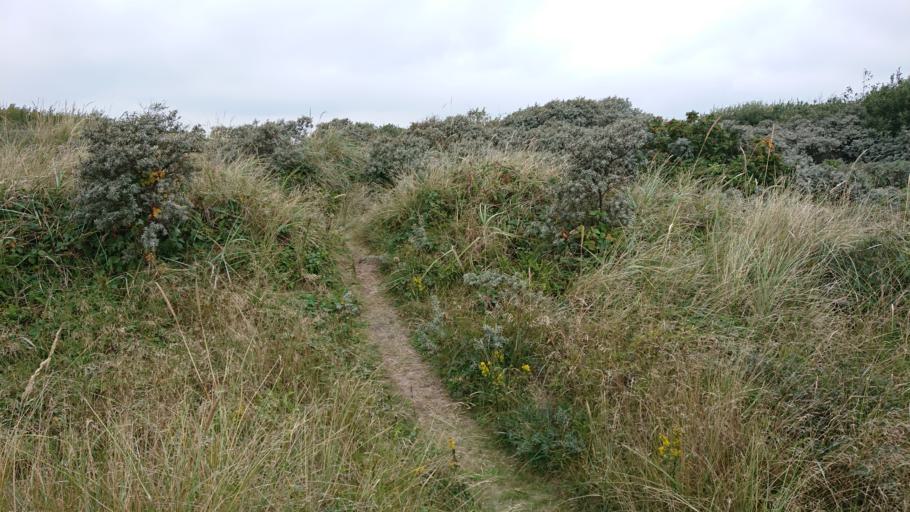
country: DK
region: North Denmark
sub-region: Frederikshavn Kommune
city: Skagen
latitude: 57.7478
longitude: 10.6215
